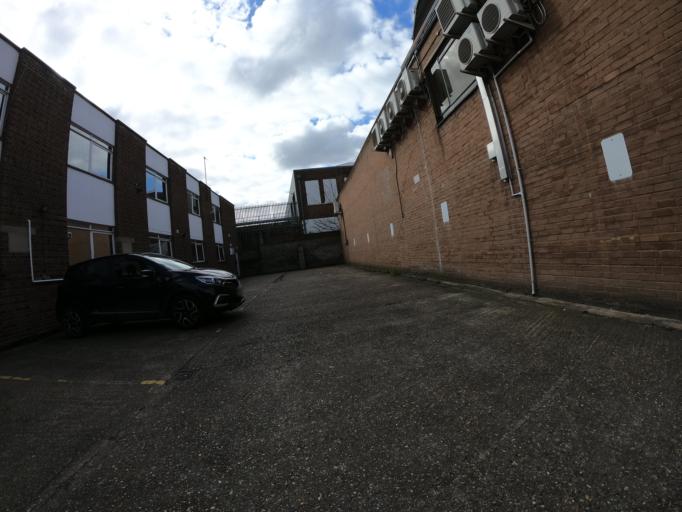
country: GB
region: England
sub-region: Greater London
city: Woolwich
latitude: 51.4925
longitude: 0.0444
